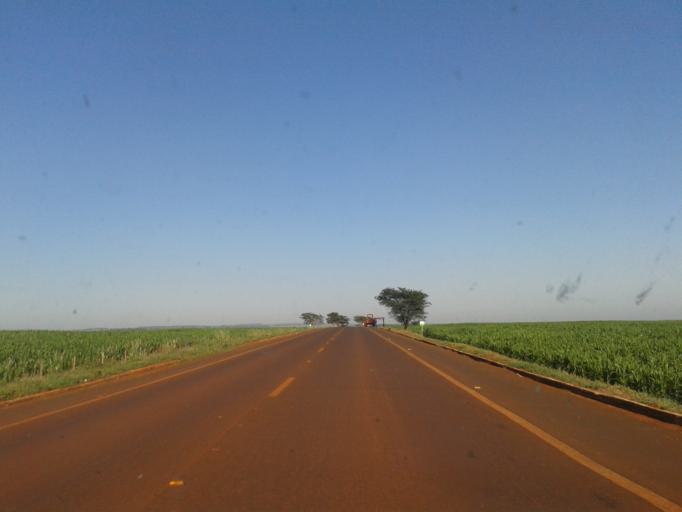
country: BR
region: Minas Gerais
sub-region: Capinopolis
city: Capinopolis
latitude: -18.6981
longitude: -49.6395
